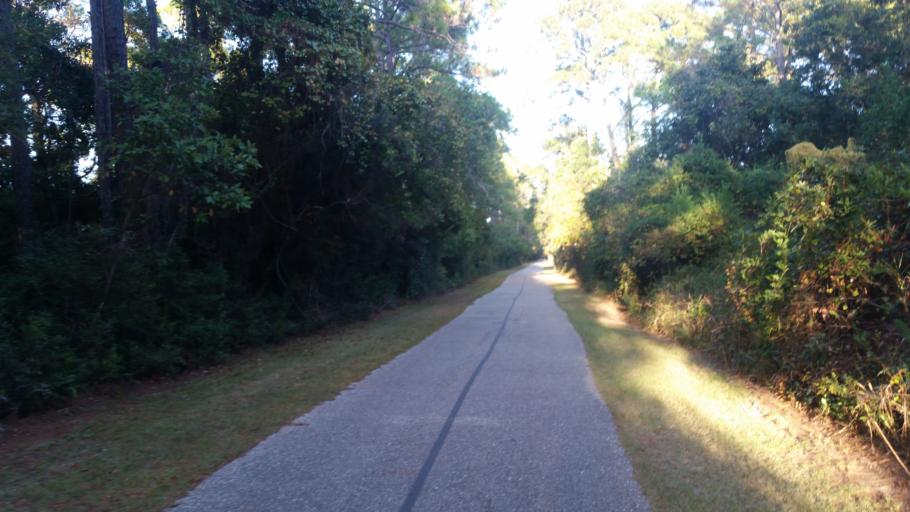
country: US
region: Alabama
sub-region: Baldwin County
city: Orange Beach
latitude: 30.2781
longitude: -87.5898
